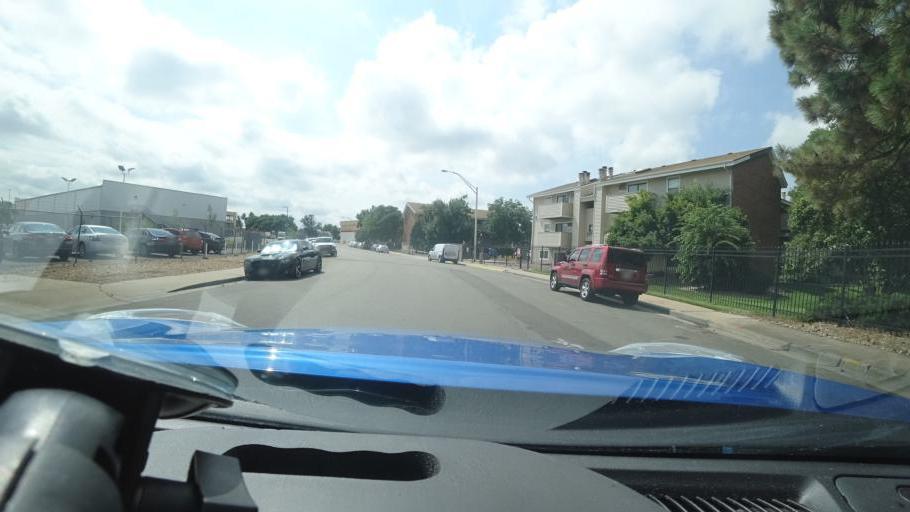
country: US
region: Colorado
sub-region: Adams County
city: Aurora
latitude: 39.7068
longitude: -104.8681
